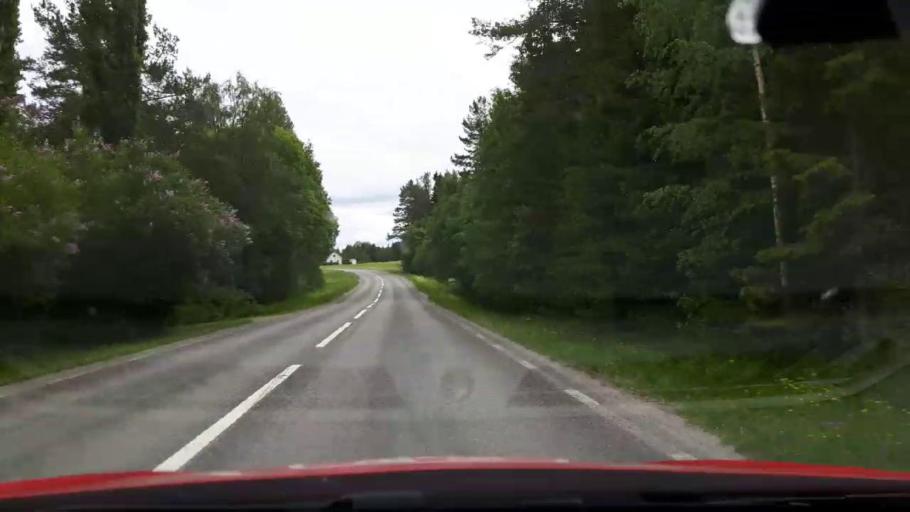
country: SE
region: Jaemtland
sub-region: Ragunda Kommun
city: Hammarstrand
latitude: 63.0927
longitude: 16.3579
